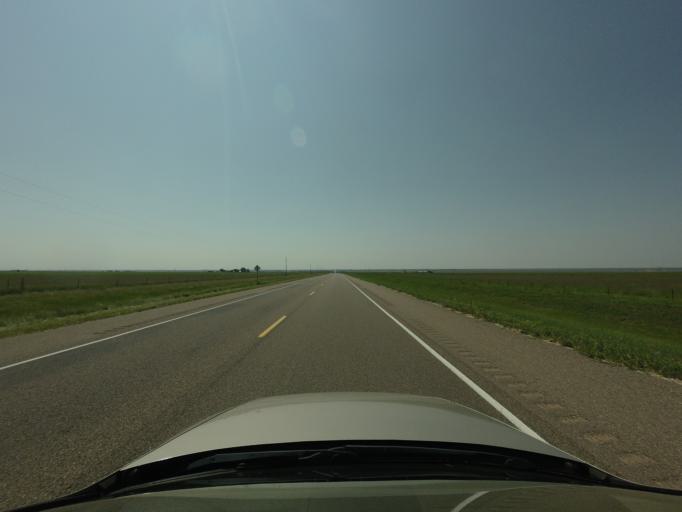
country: US
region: New Mexico
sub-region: Curry County
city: Clovis
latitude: 34.5569
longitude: -103.1966
